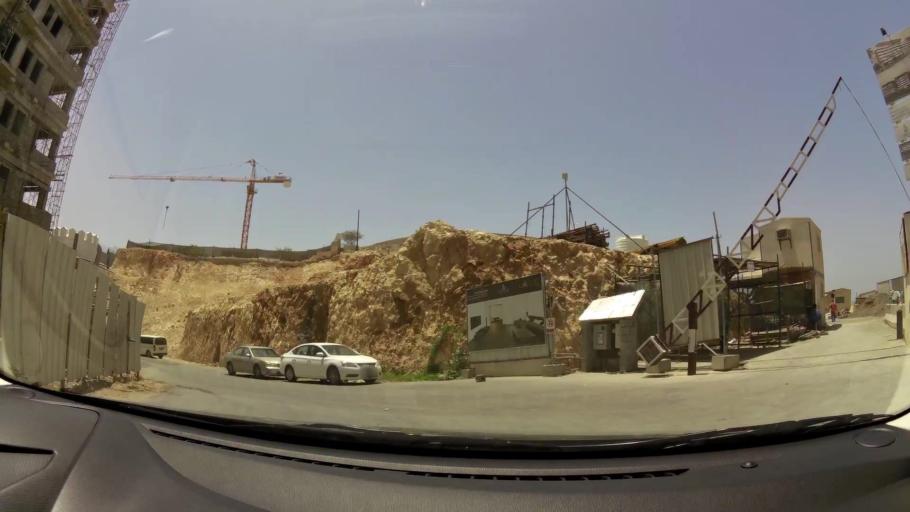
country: OM
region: Muhafazat Masqat
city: Muscat
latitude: 23.6244
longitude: 58.5029
